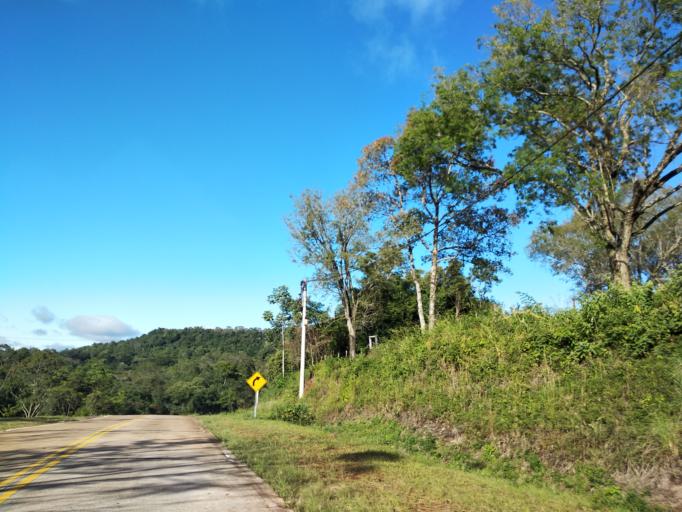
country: AR
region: Misiones
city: Cerro Cora
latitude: -27.4515
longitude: -55.5651
